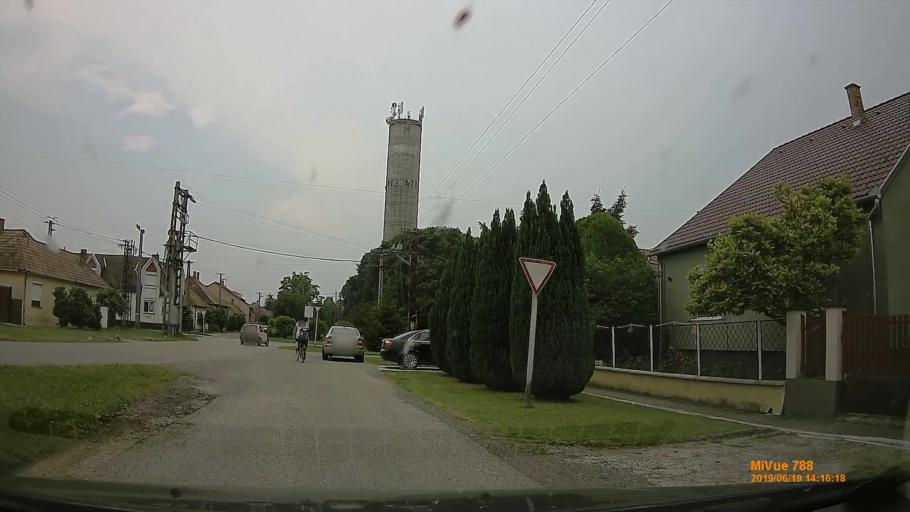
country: HU
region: Baranya
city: Szigetvar
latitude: 46.0512
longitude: 17.7845
